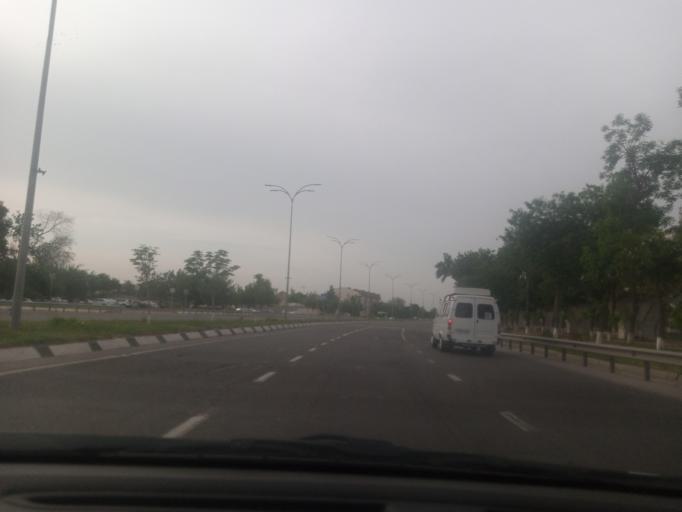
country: UZ
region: Toshkent Shahri
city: Bektemir
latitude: 41.2891
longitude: 69.3593
